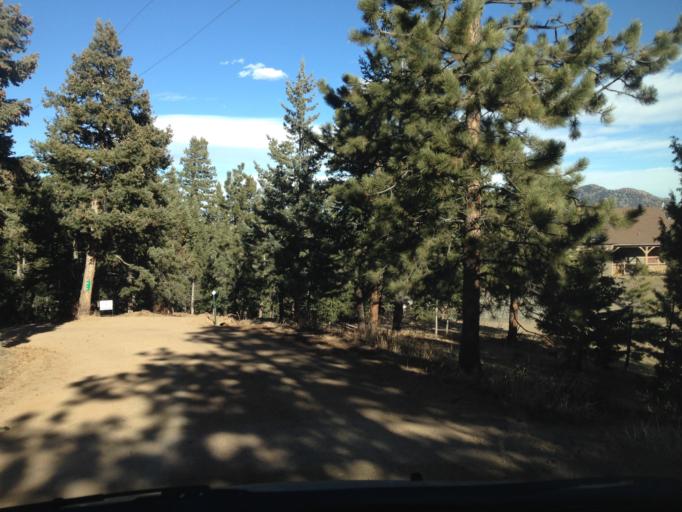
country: US
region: Colorado
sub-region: Boulder County
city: Coal Creek
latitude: 39.9217
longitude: -105.3523
